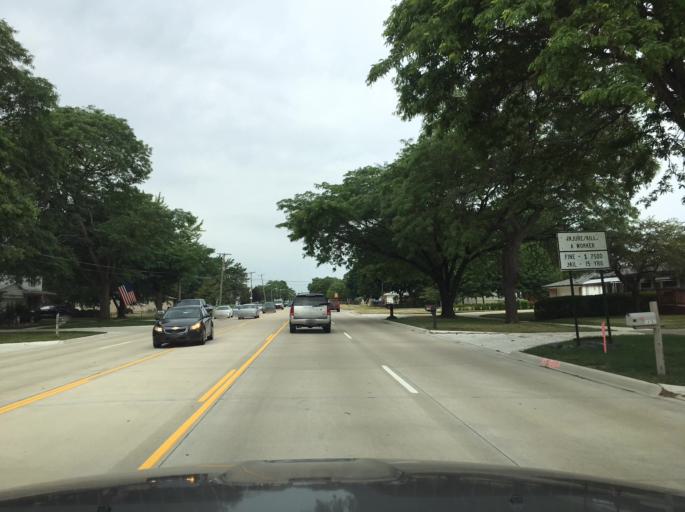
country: US
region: Michigan
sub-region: Macomb County
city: Fraser
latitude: 42.5232
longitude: -82.9738
